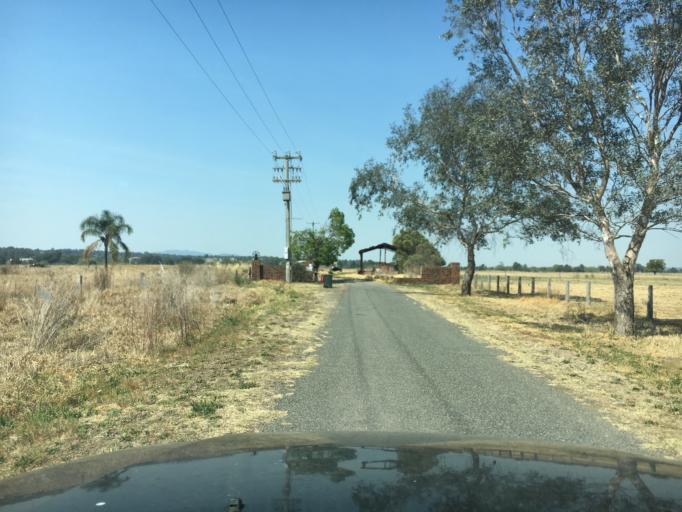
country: AU
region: New South Wales
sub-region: Singleton
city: Singleton
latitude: -32.5731
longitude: 151.1938
